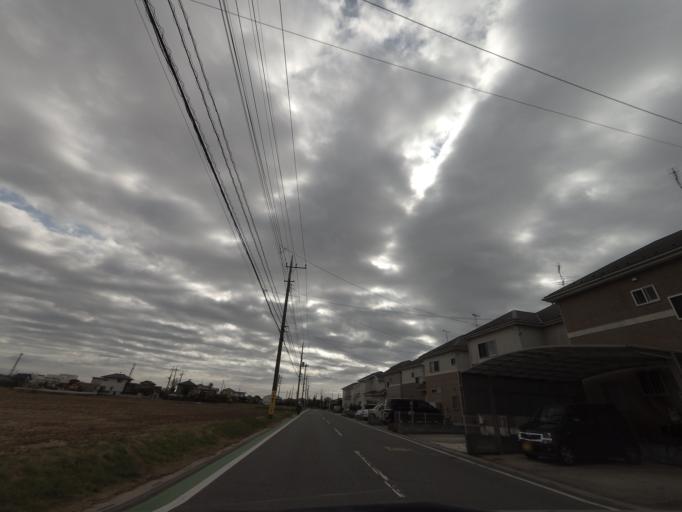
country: JP
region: Saitama
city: Kamifukuoka
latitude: 35.8915
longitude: 139.5435
